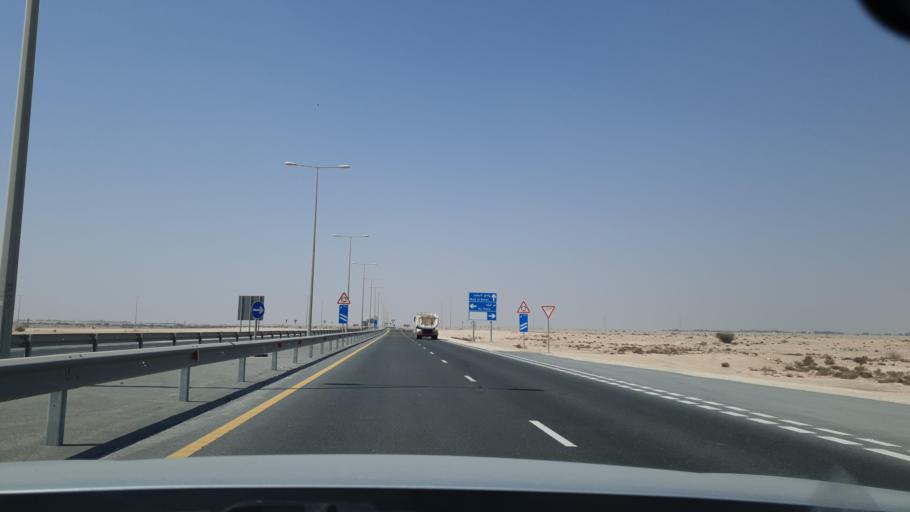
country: QA
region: Baladiyat az Za`ayin
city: Az Za`ayin
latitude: 25.6228
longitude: 51.3446
